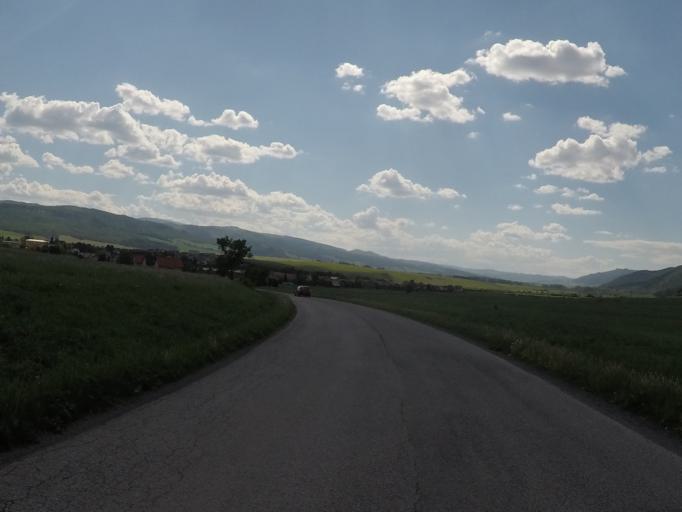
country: SK
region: Presovsky
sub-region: Okres Poprad
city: Poprad
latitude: 49.0004
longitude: 20.3667
